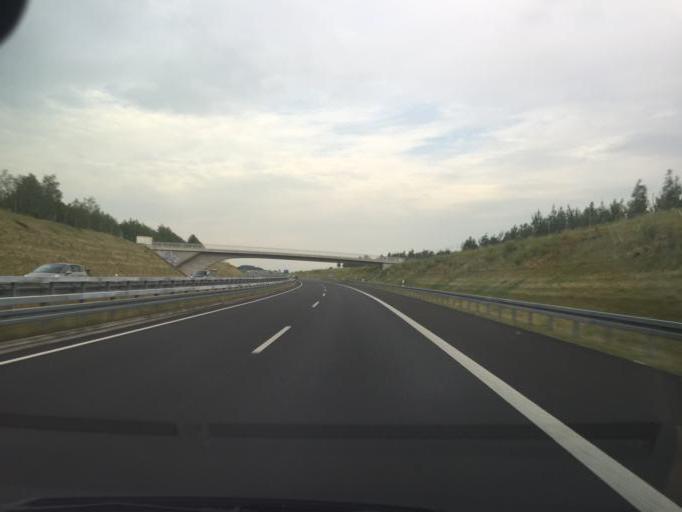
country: NL
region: Limburg
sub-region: Gemeente Venlo
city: Venlo
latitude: 51.3320
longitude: 6.1775
